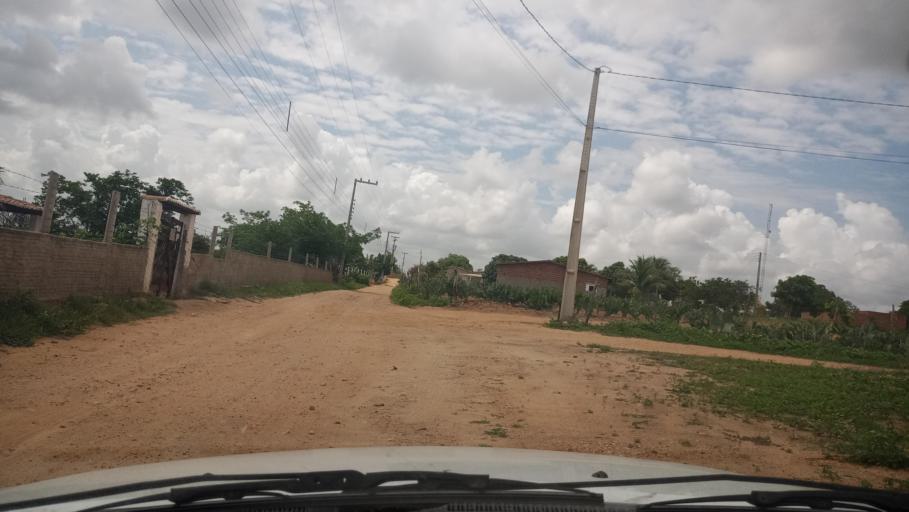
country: BR
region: Rio Grande do Norte
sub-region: Sao Paulo Do Potengi
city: Sao Paulo do Potengi
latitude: -5.9141
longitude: -35.6950
